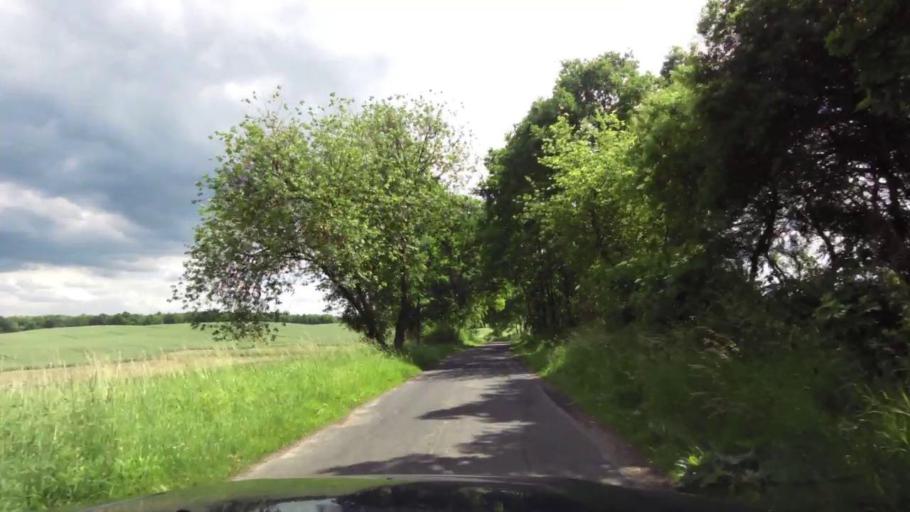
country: PL
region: West Pomeranian Voivodeship
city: Trzcinsko Zdroj
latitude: 52.9054
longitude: 14.6045
